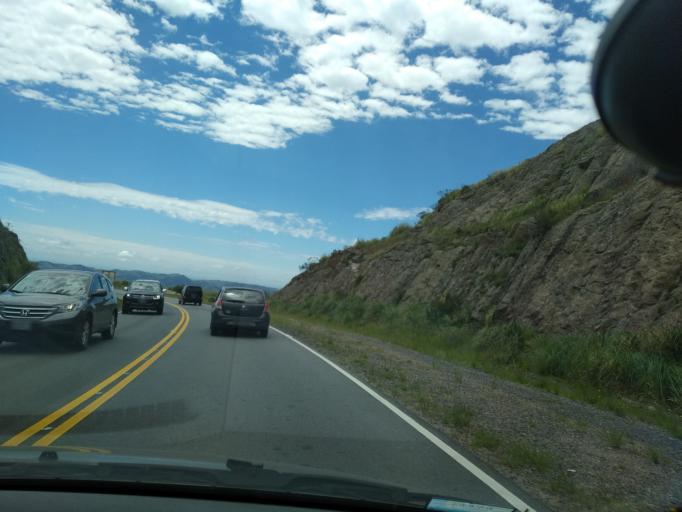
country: AR
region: Cordoba
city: Cuesta Blanca
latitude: -31.6383
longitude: -64.6784
